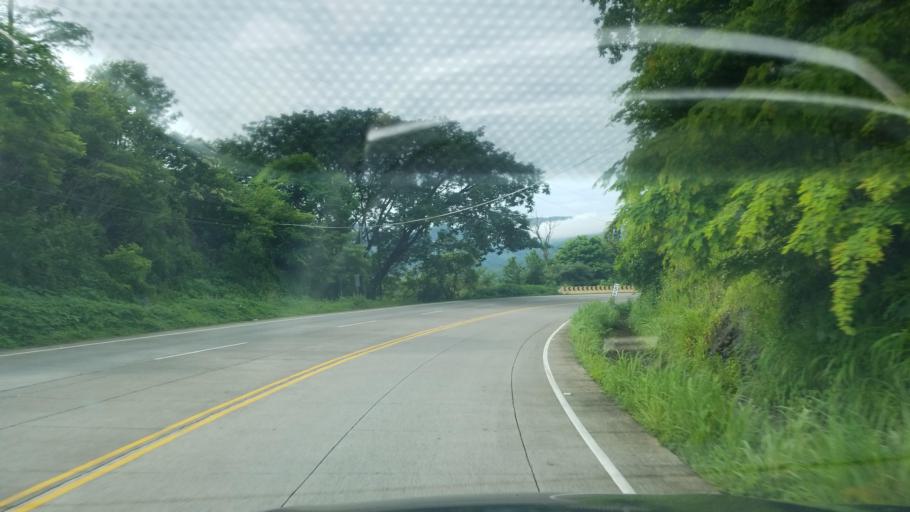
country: HN
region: Francisco Morazan
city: El Porvenir
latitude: 13.7038
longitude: -87.3159
